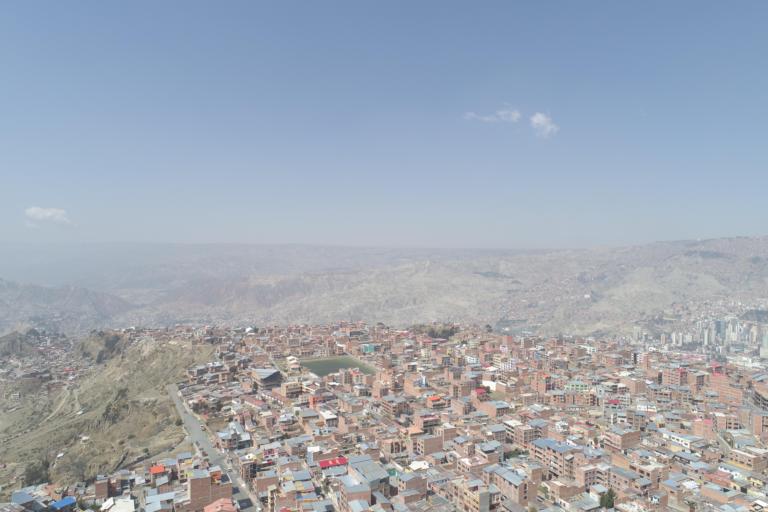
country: BO
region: La Paz
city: La Paz
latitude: -16.4960
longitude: -68.1011
